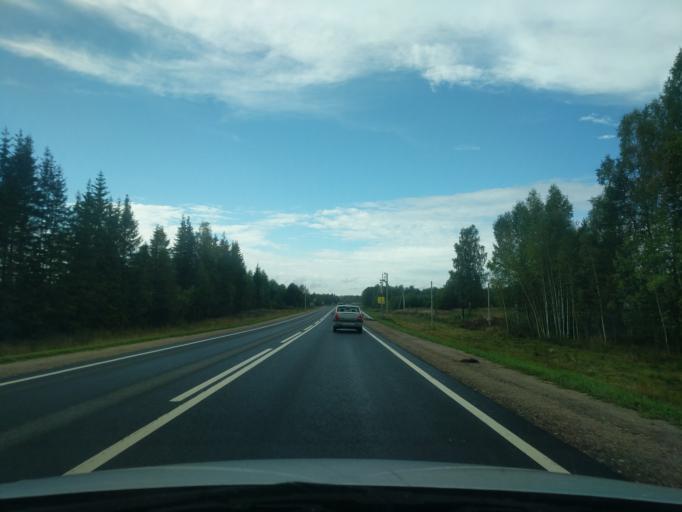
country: RU
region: Kostroma
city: Ostrovskoye
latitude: 57.8140
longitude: 41.9954
